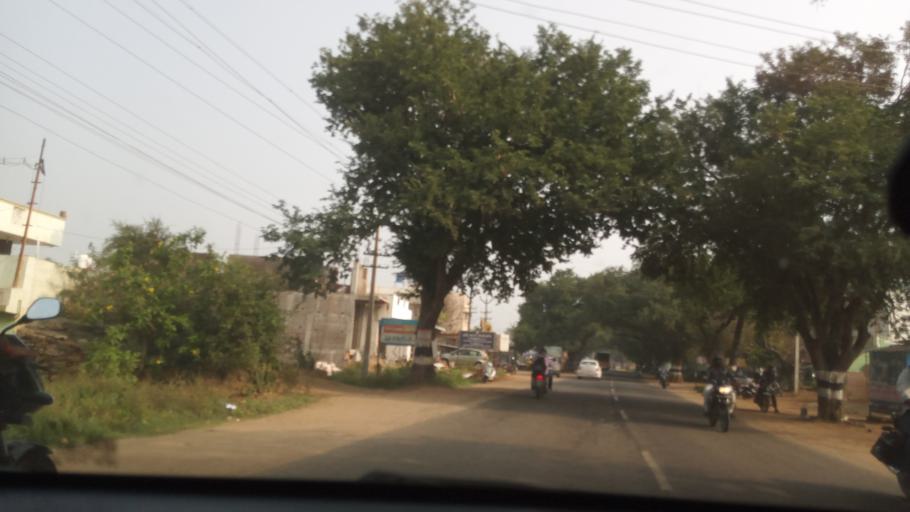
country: IN
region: Tamil Nadu
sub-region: Coimbatore
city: Annur
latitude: 11.1686
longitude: 77.0534
